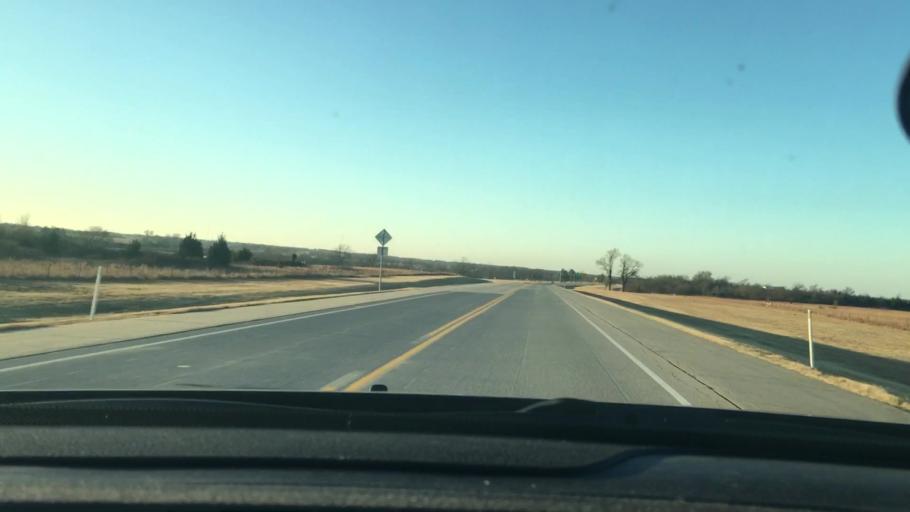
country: US
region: Oklahoma
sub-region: Murray County
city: Sulphur
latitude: 34.5755
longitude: -96.9251
